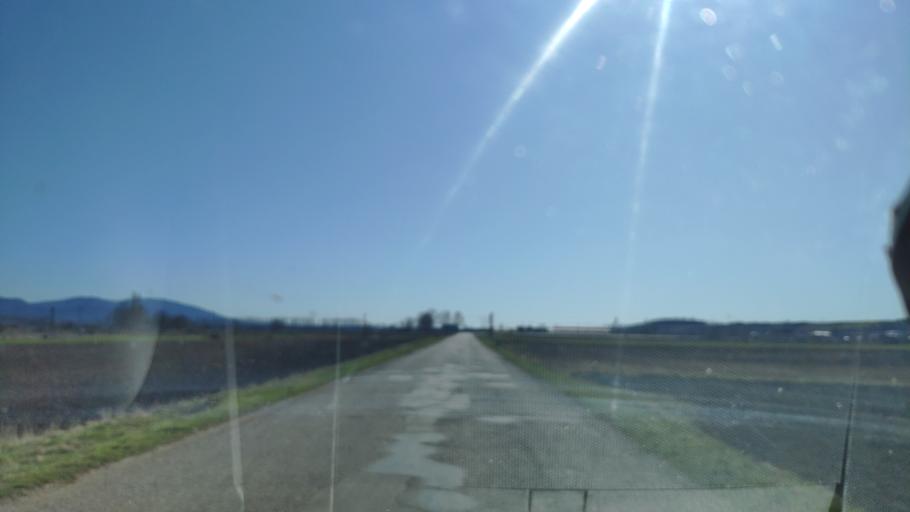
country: HU
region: Borsod-Abauj-Zemplen
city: Gonc
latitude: 48.5916
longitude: 21.3127
